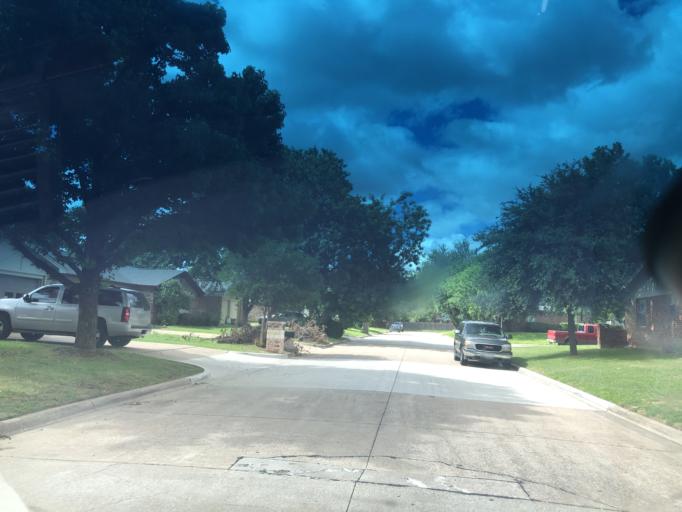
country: US
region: Texas
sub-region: Dallas County
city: Grand Prairie
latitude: 32.7083
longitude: -97.0367
